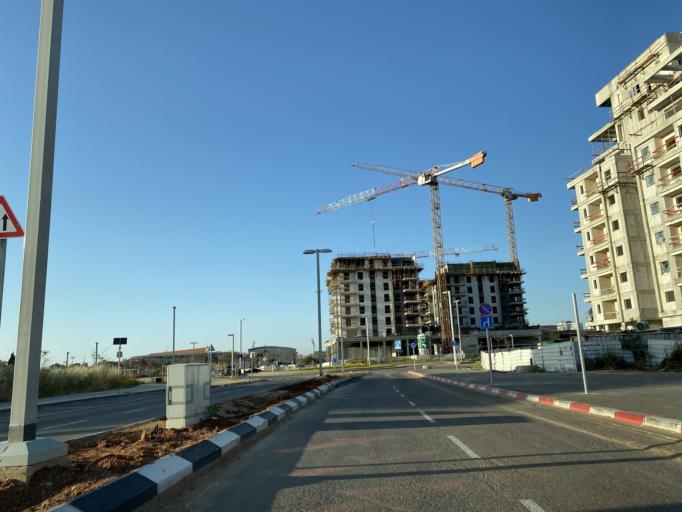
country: IL
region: Tel Aviv
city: Herzliyya
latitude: 32.1606
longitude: 34.8237
